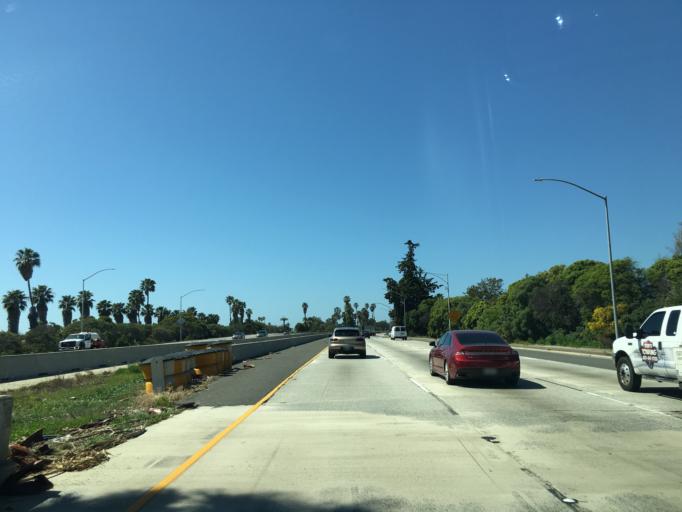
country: US
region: California
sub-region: Ventura County
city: Ventura
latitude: 34.2776
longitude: -119.2979
